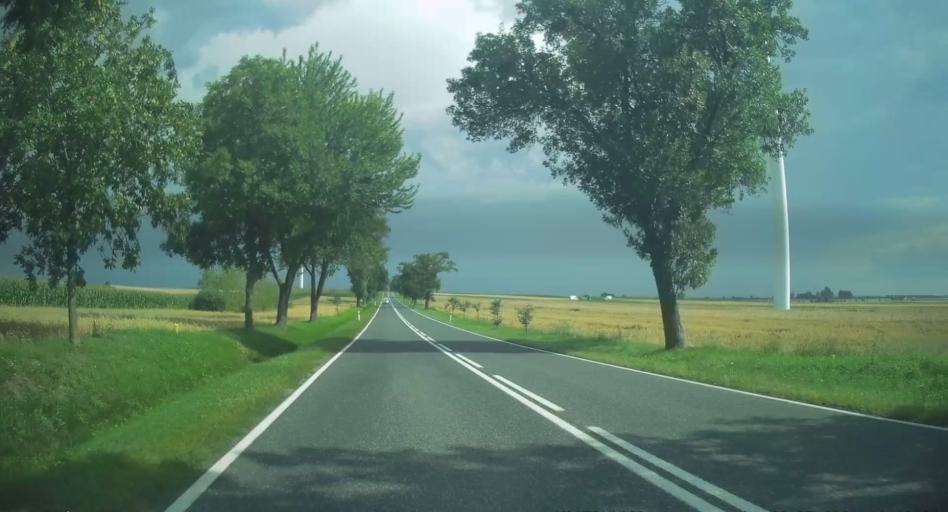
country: PL
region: Lodz Voivodeship
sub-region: Powiat skierniewicki
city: Gluchow
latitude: 51.7931
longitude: 20.0379
